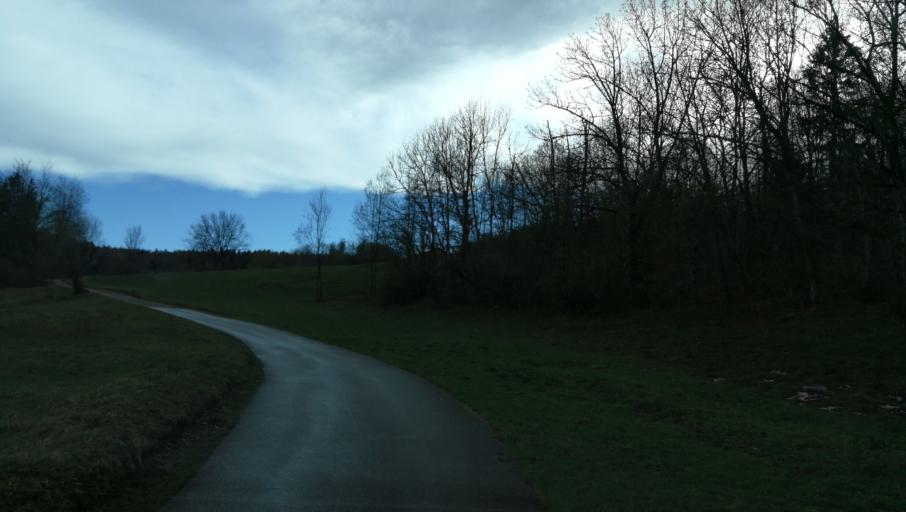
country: FR
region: Franche-Comte
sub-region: Departement du Jura
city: Lavans-les-Saint-Claude
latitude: 46.3170
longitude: 5.8073
